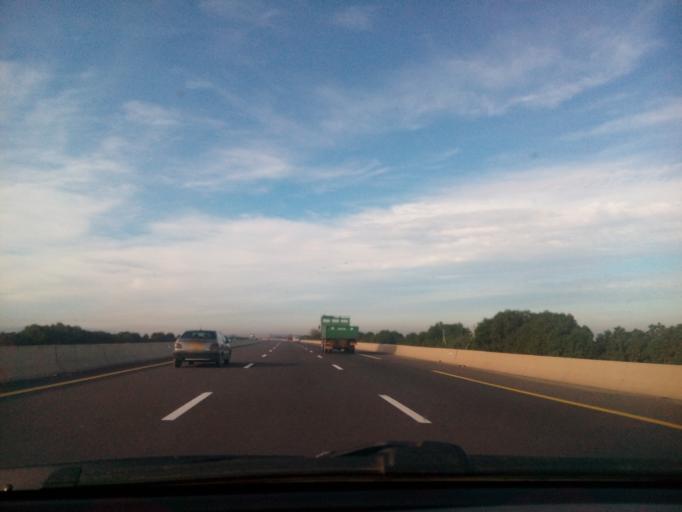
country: DZ
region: Mascara
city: Sig
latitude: 35.5907
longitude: -0.0683
